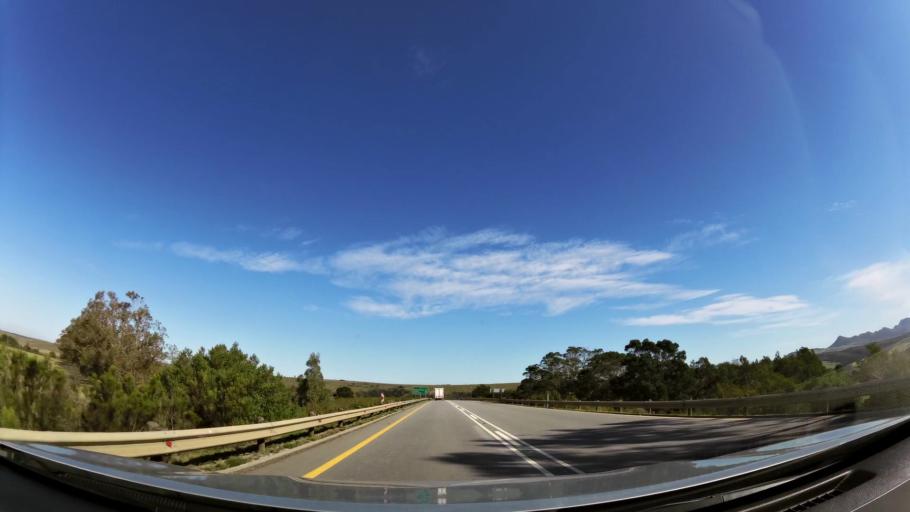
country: ZA
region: Eastern Cape
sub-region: Cacadu District Municipality
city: Kruisfontein
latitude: -34.0360
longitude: 24.5921
